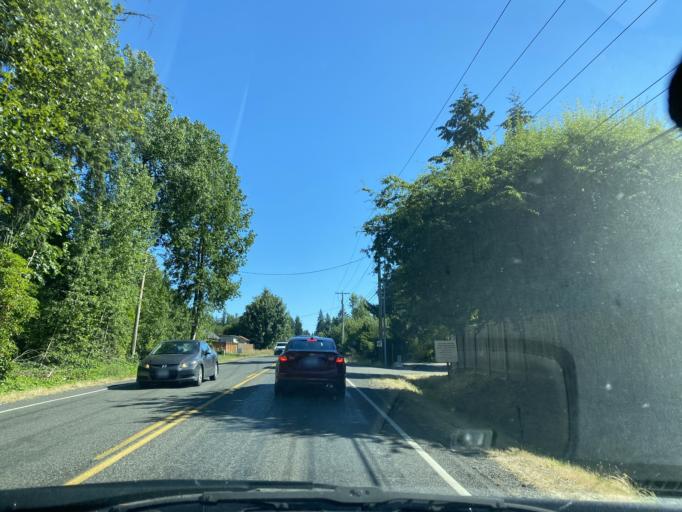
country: US
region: Washington
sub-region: Pierce County
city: South Hill
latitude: 47.1489
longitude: -122.2586
